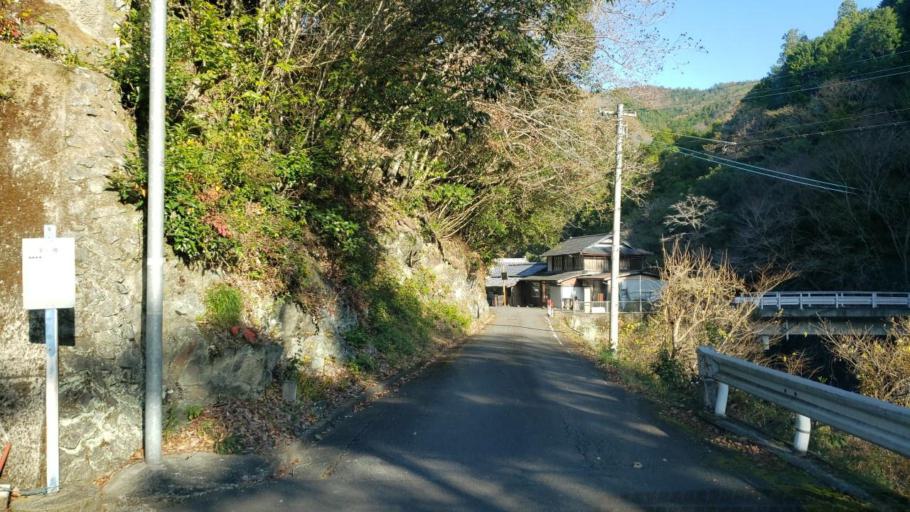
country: JP
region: Tokushima
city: Wakimachi
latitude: 34.0204
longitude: 134.0382
